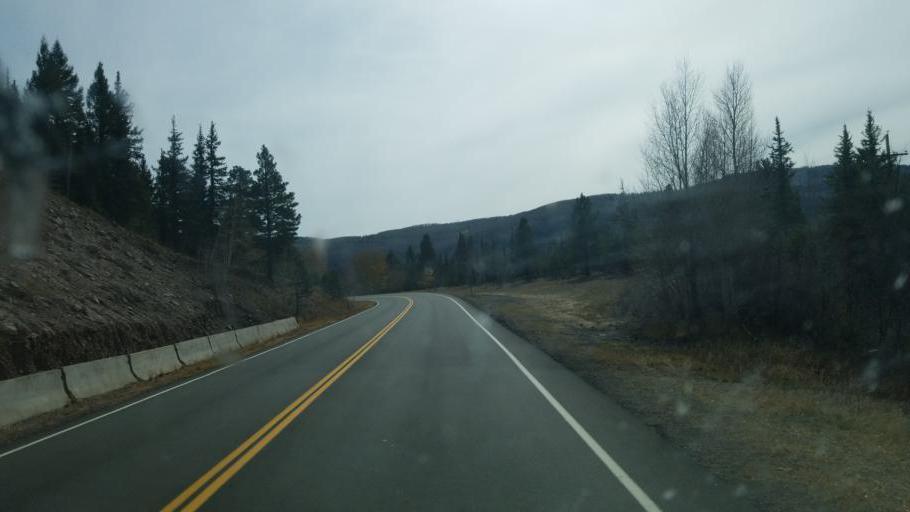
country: US
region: Colorado
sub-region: Conejos County
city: Conejos
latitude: 37.0886
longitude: -106.3024
